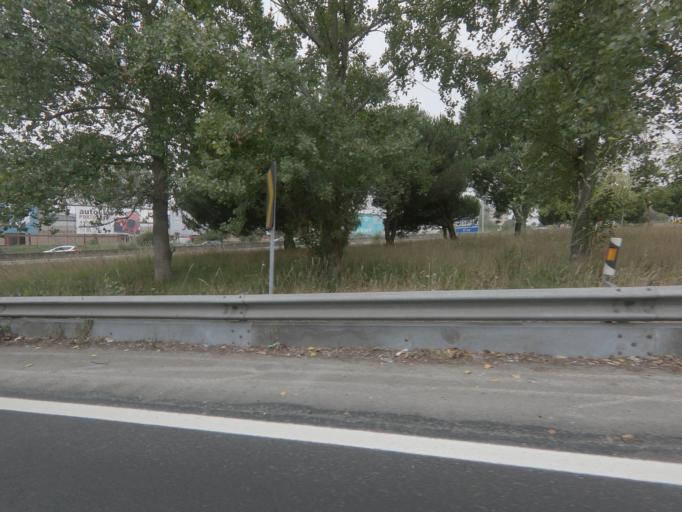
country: PT
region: Porto
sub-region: Matosinhos
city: Leca da Palmeira
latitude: 41.2016
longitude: -8.6886
